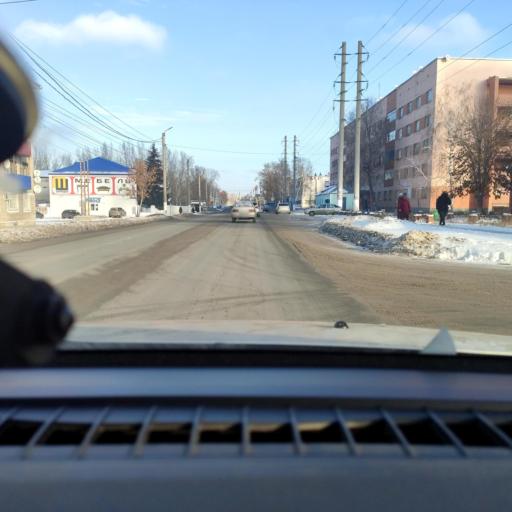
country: RU
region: Samara
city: Chapayevsk
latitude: 52.9719
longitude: 49.7065
